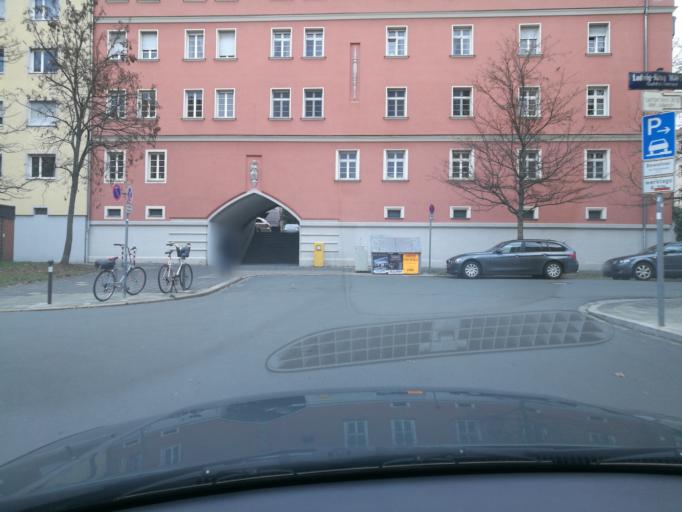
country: DE
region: Bavaria
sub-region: Regierungsbezirk Mittelfranken
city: Wetzendorf
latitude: 49.4592
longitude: 11.0537
